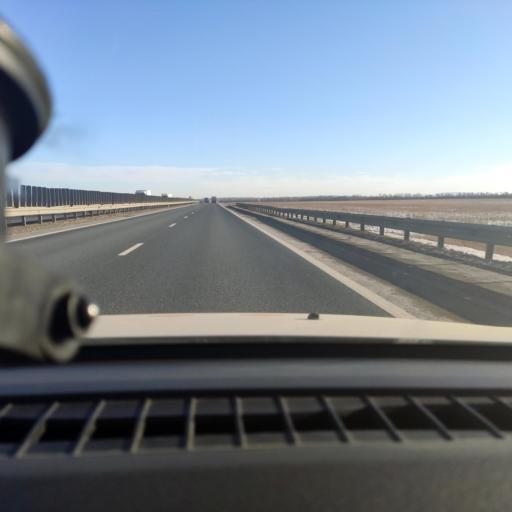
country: RU
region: Samara
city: Kurumoch
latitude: 53.5077
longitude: 49.9651
